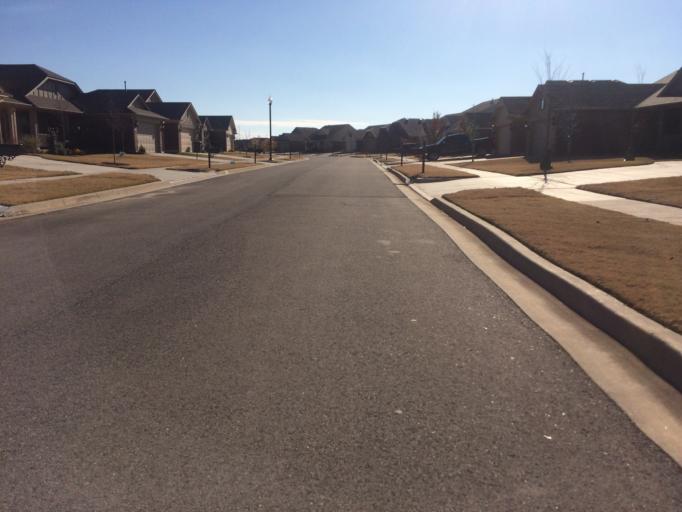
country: US
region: Oklahoma
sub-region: Cleveland County
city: Norman
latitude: 35.2509
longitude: -97.4555
